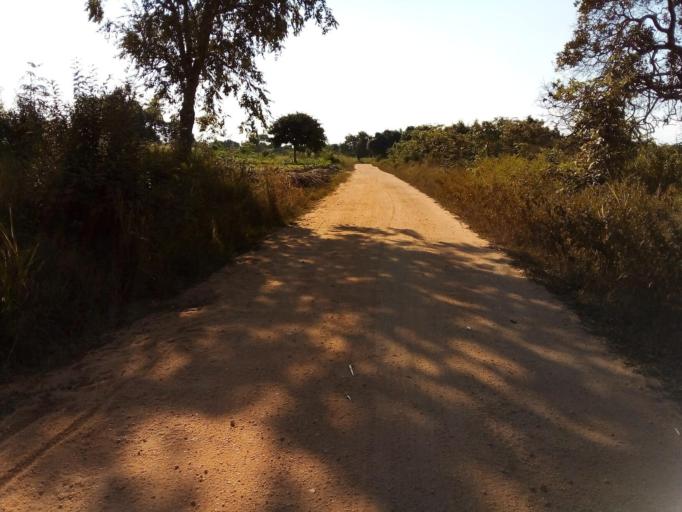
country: MZ
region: Zambezia
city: Quelimane
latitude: -17.5423
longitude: 36.6261
